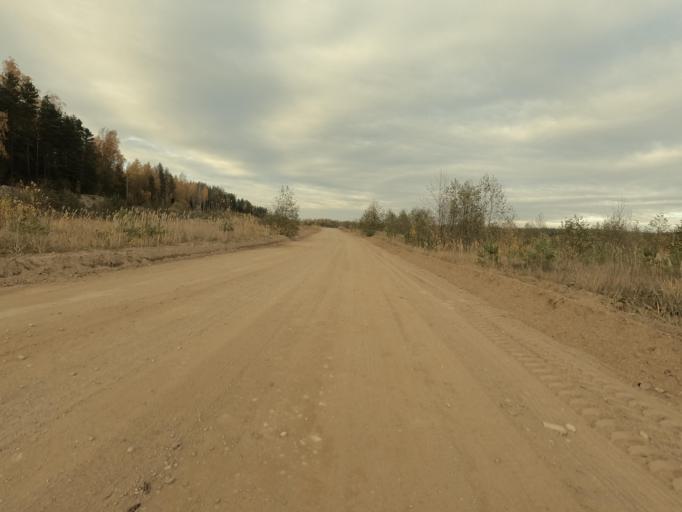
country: RU
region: Leningrad
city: Priladozhskiy
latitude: 59.7045
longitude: 31.3642
